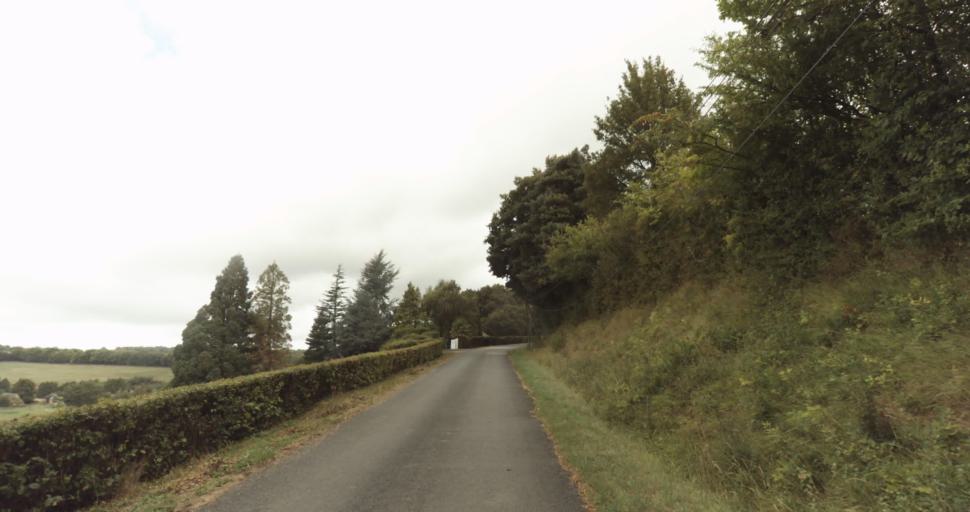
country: FR
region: Lower Normandy
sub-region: Departement de l'Orne
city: Gace
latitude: 48.8272
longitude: 0.2565
